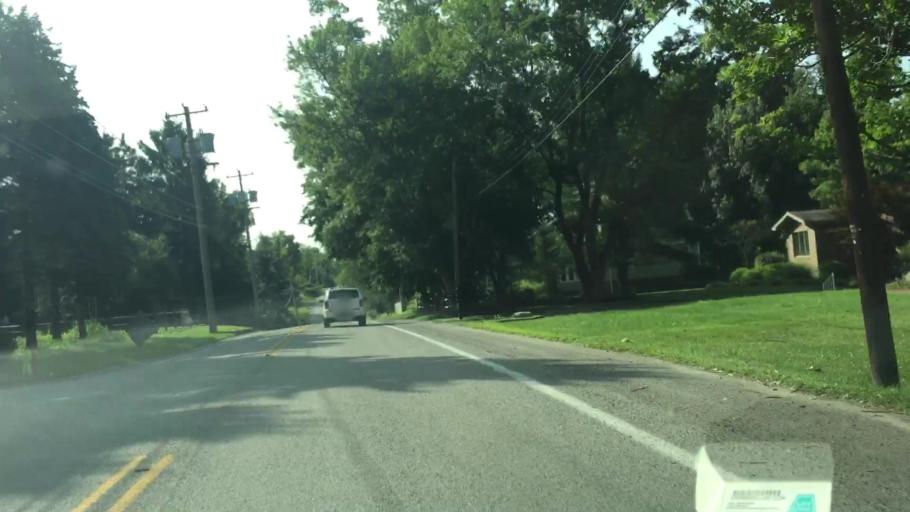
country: US
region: Pennsylvania
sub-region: Allegheny County
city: Oakmont
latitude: 40.5163
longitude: -79.8605
